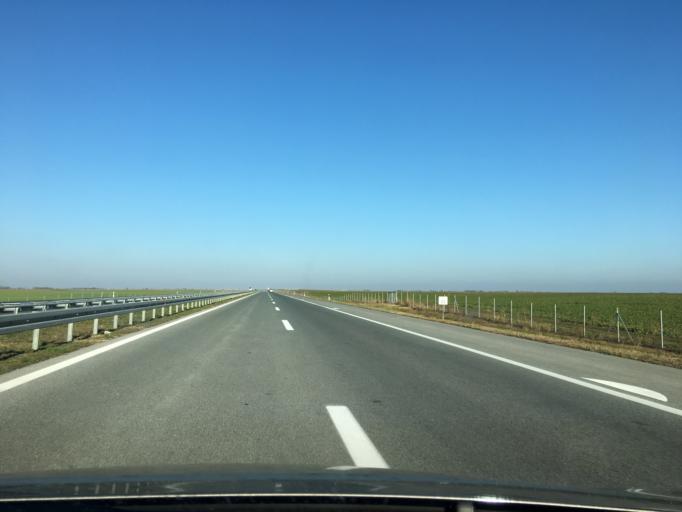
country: RS
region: Autonomna Pokrajina Vojvodina
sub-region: Severnobacki Okrug
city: Mali Igos
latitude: 45.7101
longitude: 19.7153
